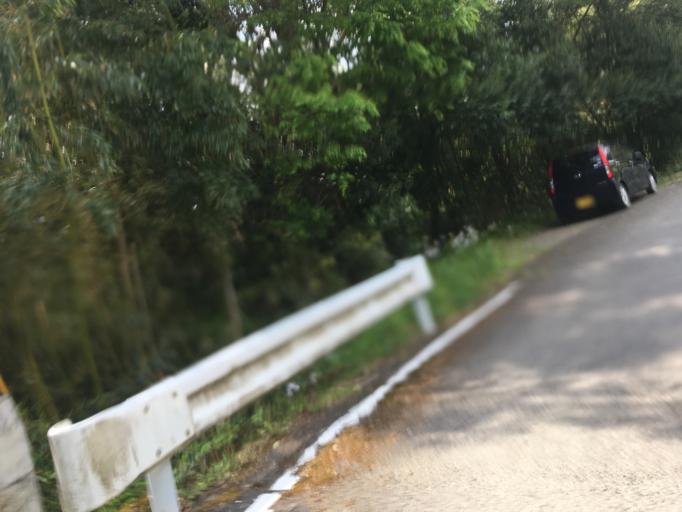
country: JP
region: Kyoto
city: Kameoka
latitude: 35.0861
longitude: 135.6116
